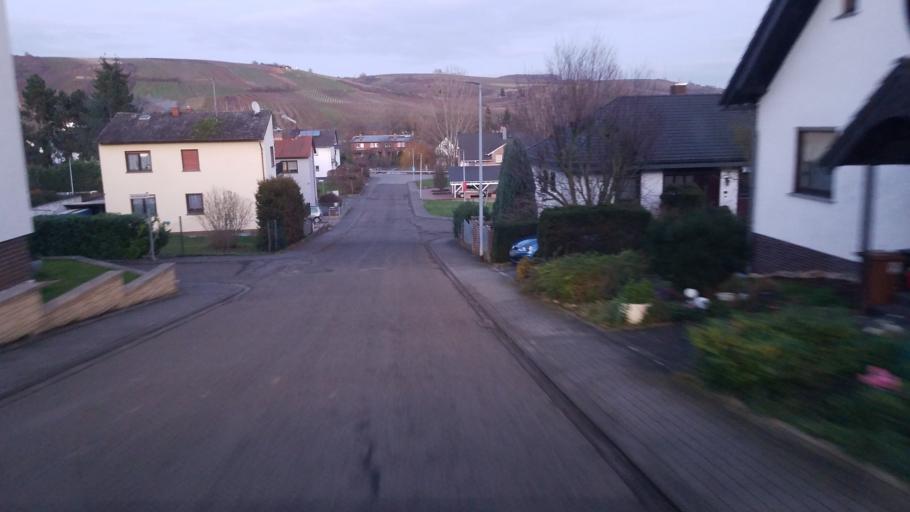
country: DE
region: Rheinland-Pfalz
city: Windesheim
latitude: 49.8925
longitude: 7.8353
